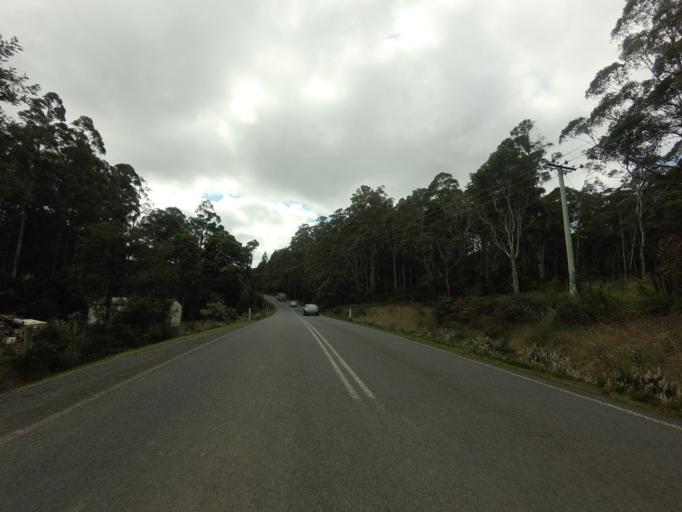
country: AU
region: Tasmania
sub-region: Huon Valley
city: Cygnet
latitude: -43.2731
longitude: 147.0106
